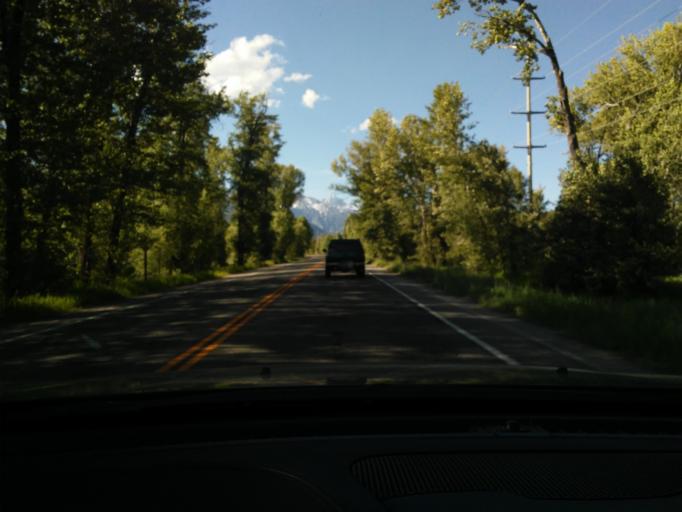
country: US
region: Wyoming
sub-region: Teton County
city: Moose Wilson Road
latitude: 43.5434
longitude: -110.8221
